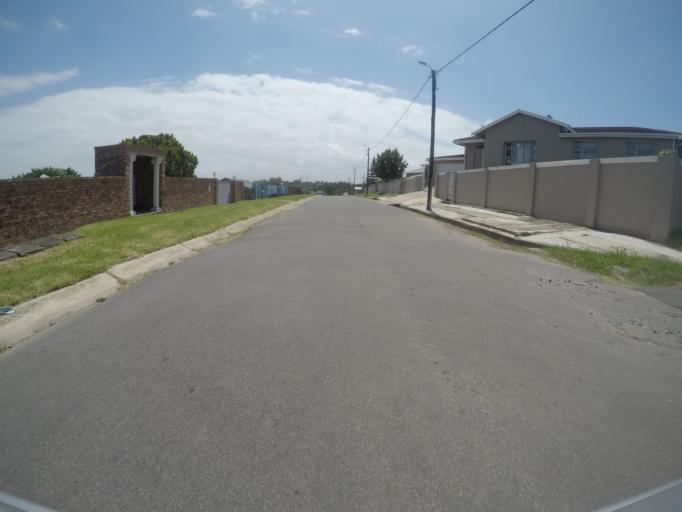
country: ZA
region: Eastern Cape
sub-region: Buffalo City Metropolitan Municipality
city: East London
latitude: -32.9717
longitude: 27.8663
